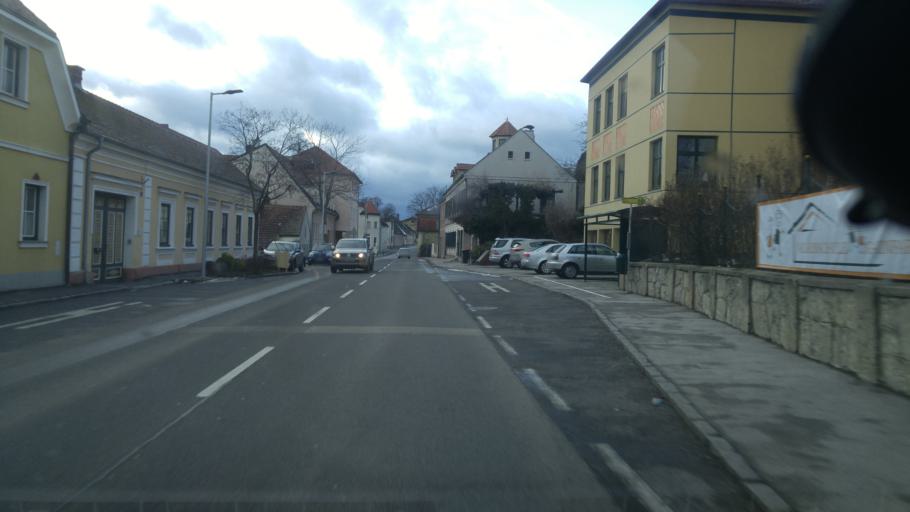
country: AT
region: Lower Austria
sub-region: Politischer Bezirk Baden
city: Bad Voslau
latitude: 47.9630
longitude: 16.1955
